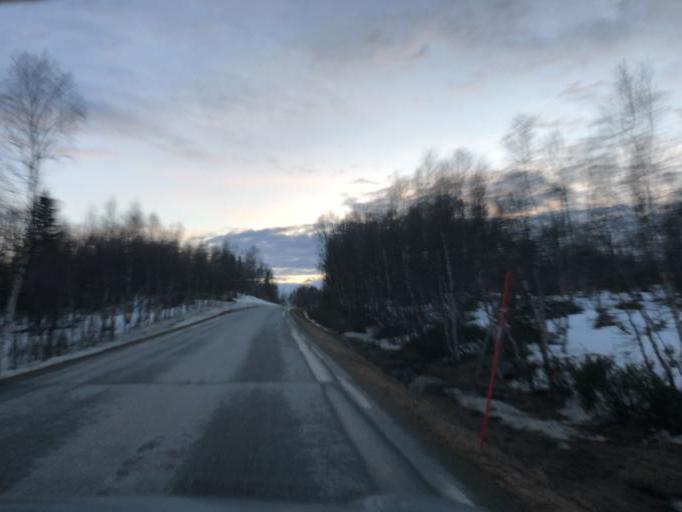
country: NO
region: Sor-Trondelag
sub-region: Tydal
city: Aas
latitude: 62.6726
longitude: 11.8172
